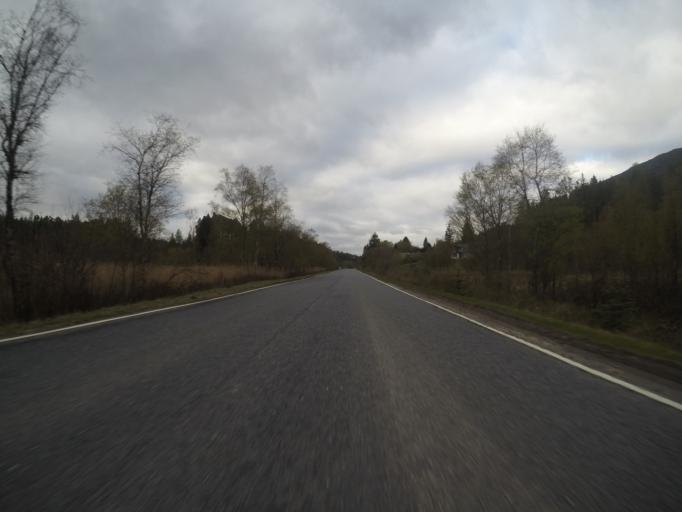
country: GB
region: Scotland
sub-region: Highland
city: Kingussie
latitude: 56.9839
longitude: -4.3523
